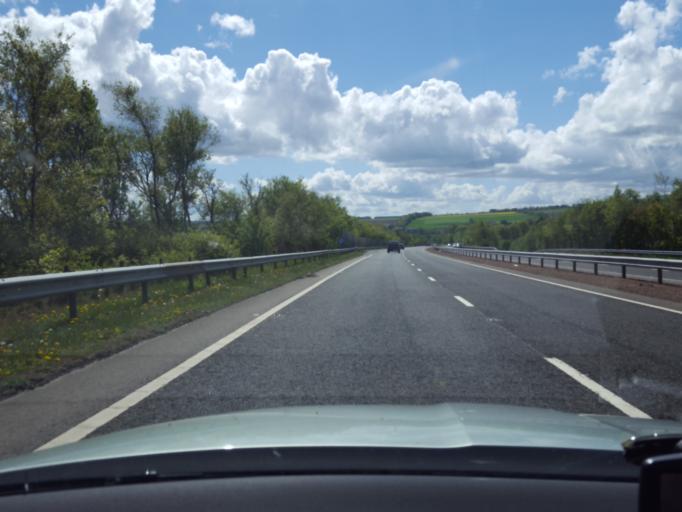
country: GB
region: Scotland
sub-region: Angus
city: Forfar
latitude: 56.6052
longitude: -2.9030
